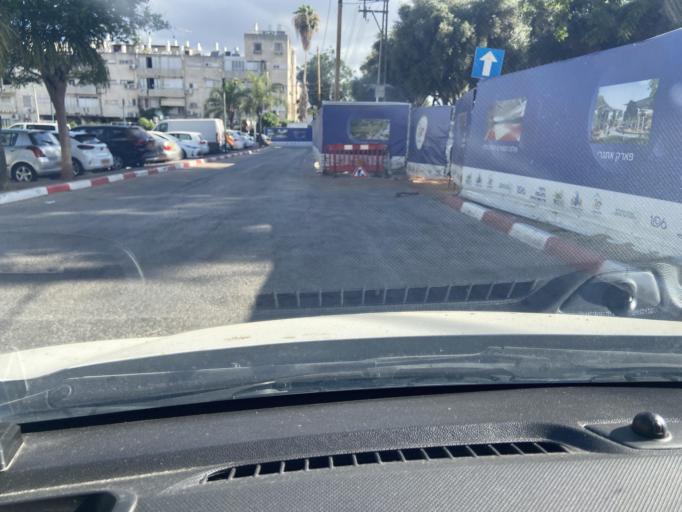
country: IL
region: Central District
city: Yehud
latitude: 32.0307
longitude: 34.8898
